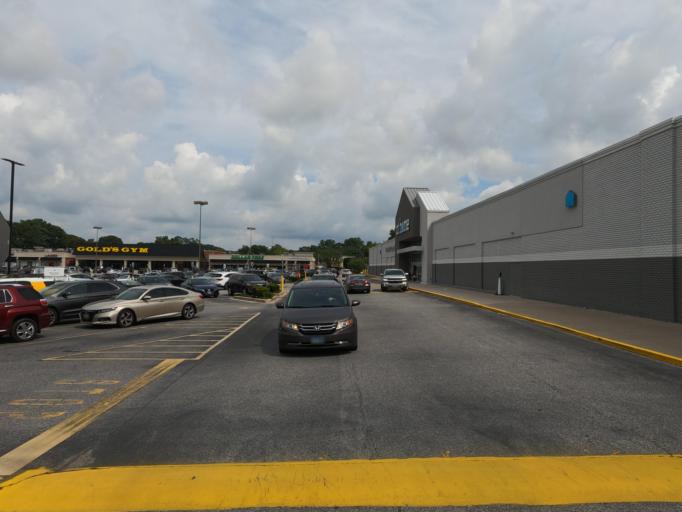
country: US
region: Maryland
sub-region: Anne Arundel County
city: Crofton
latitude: 39.0159
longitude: -76.6942
